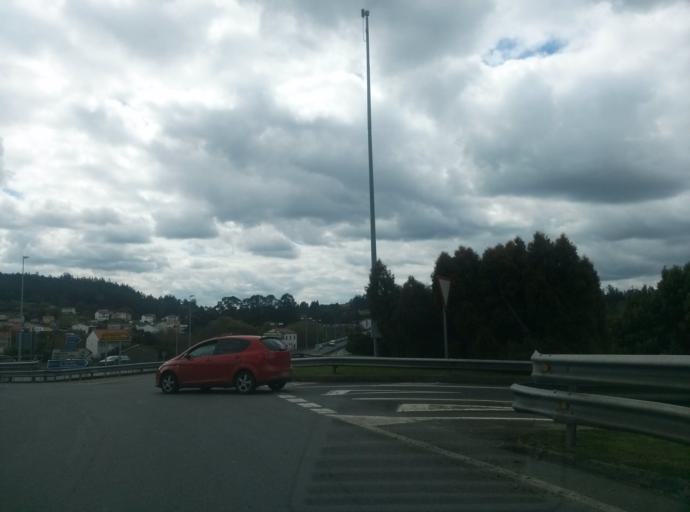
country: ES
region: Galicia
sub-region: Provincia da Coruna
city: Santiago de Compostela
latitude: 42.8640
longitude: -8.5679
